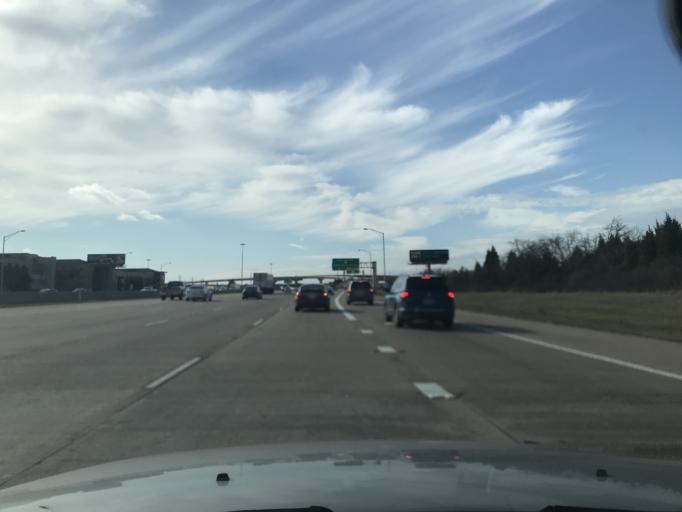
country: US
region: Texas
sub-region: Dallas County
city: Addison
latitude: 33.0129
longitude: -96.8222
